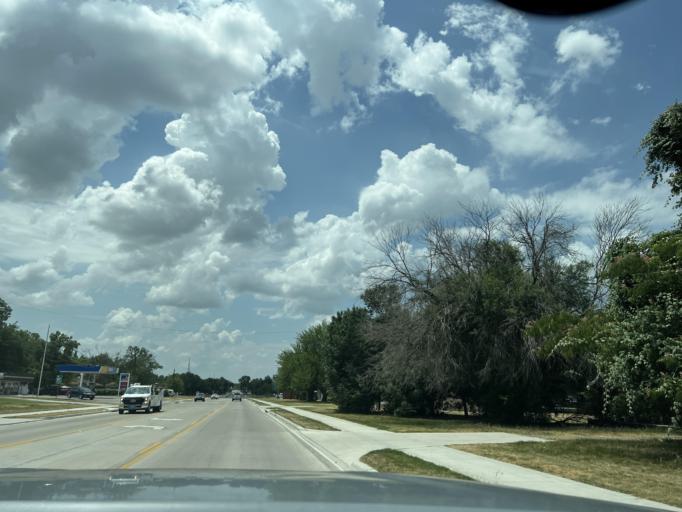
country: US
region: Texas
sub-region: Parker County
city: Springtown
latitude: 32.9747
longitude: -97.6857
